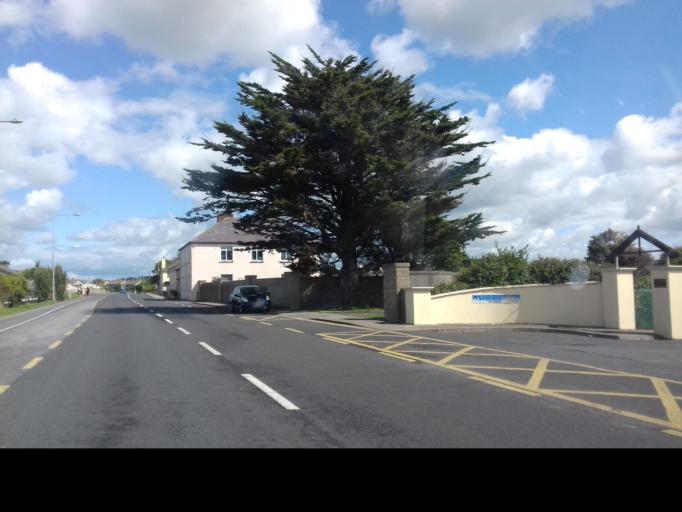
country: IE
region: Munster
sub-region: Waterford
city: Tra Mhor
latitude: 52.1631
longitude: -7.1398
